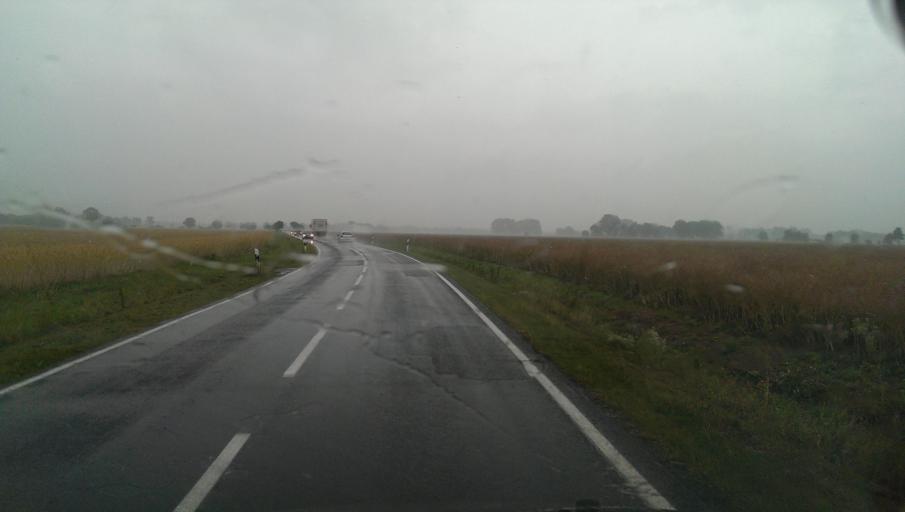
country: DE
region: Brandenburg
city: Roskow
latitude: 52.4645
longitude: 12.6824
